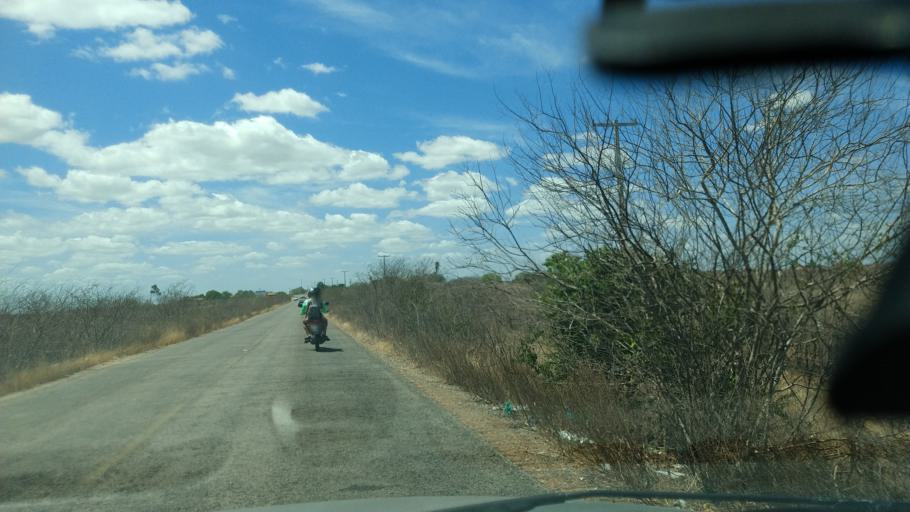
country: BR
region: Rio Grande do Norte
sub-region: Sao Paulo Do Potengi
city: Sao Paulo do Potengi
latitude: -5.9140
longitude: -35.7484
